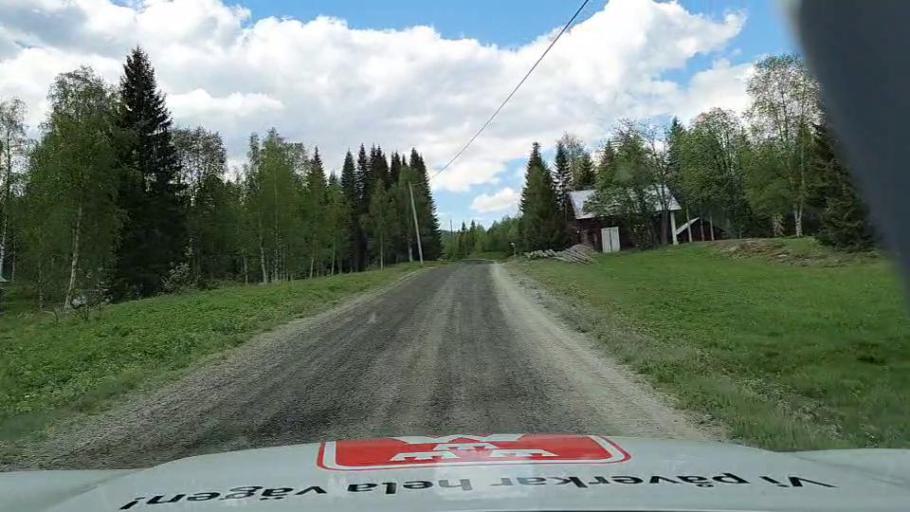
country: SE
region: Jaemtland
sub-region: Krokoms Kommun
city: Valla
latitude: 63.9656
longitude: 14.1212
